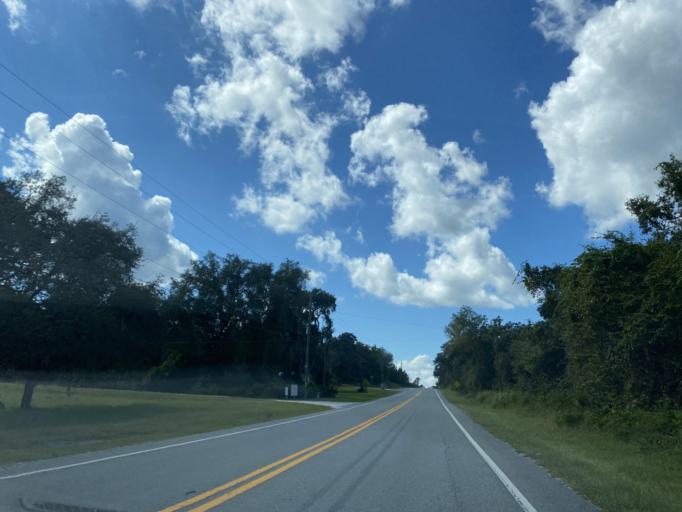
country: US
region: Florida
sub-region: Lake County
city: Lake Mack-Forest Hills
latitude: 29.0039
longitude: -81.4235
